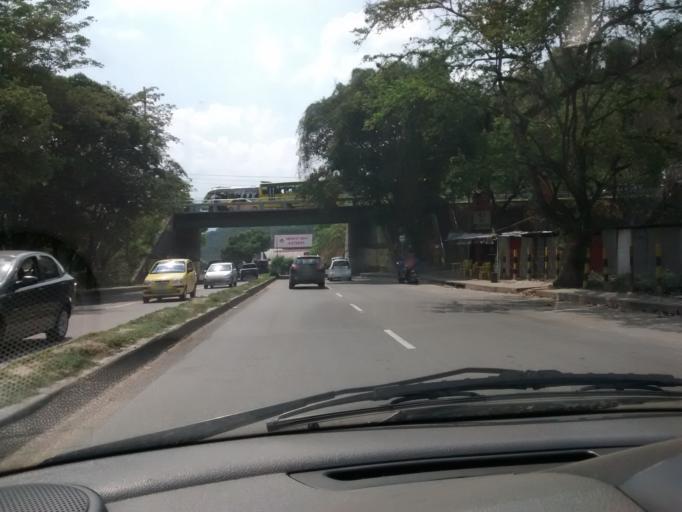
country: CO
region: Santander
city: Bucaramanga
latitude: 7.0890
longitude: -73.1327
